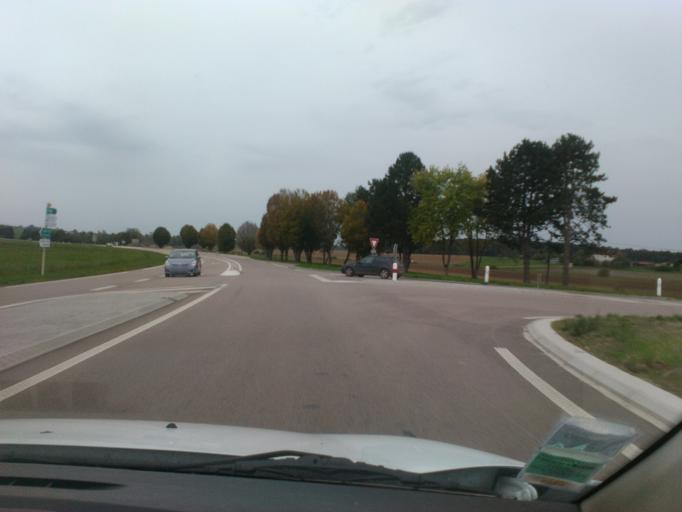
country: FR
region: Lorraine
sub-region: Departement des Vosges
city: Rambervillers
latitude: 48.3257
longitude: 6.6326
